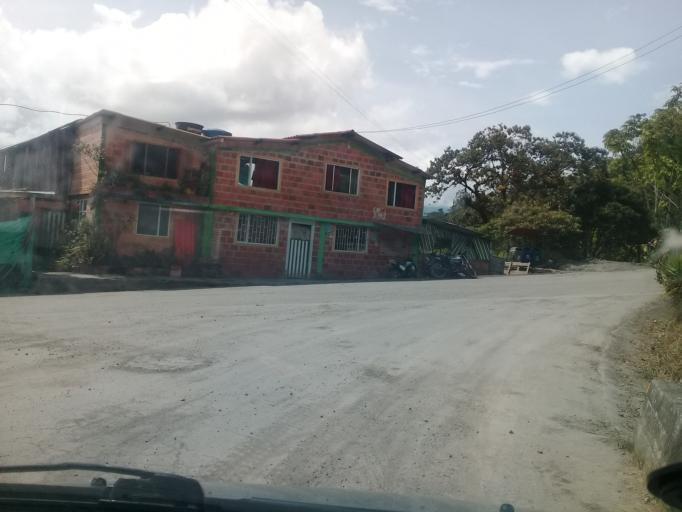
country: CO
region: Cundinamarca
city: Gachala
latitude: 4.7055
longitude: -73.4954
